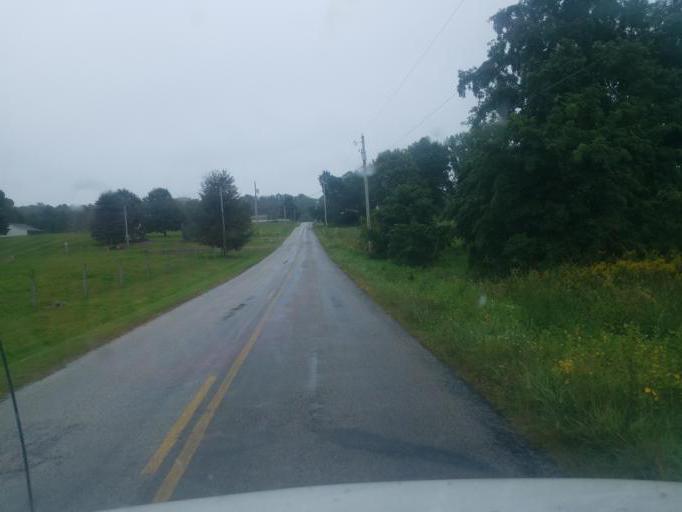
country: US
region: Ohio
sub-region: Medina County
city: Seville
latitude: 40.9824
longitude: -81.8450
